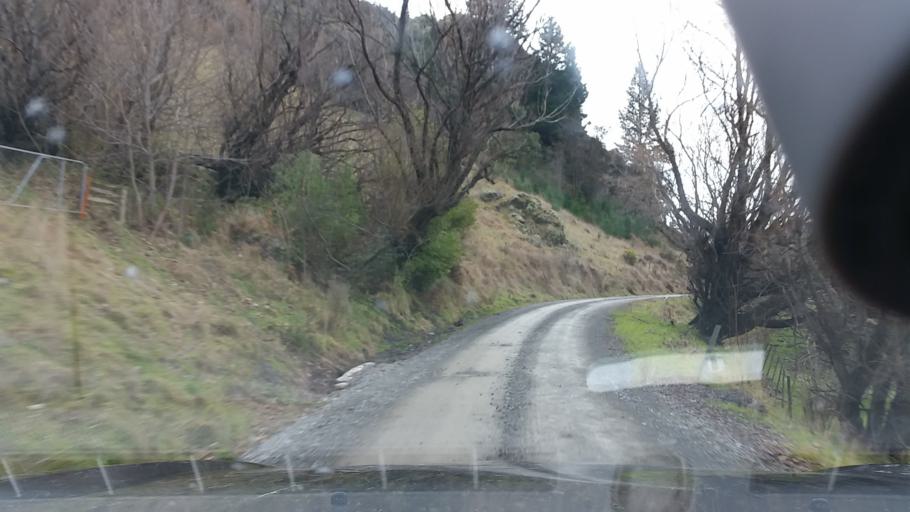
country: NZ
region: Tasman
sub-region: Tasman District
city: Richmond
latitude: -41.7212
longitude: 173.4704
